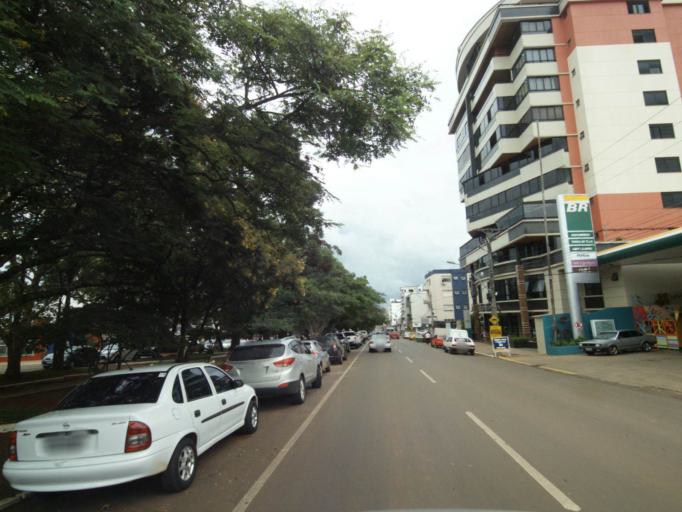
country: BR
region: Rio Grande do Sul
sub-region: Lagoa Vermelha
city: Lagoa Vermelha
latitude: -28.2110
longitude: -51.5209
